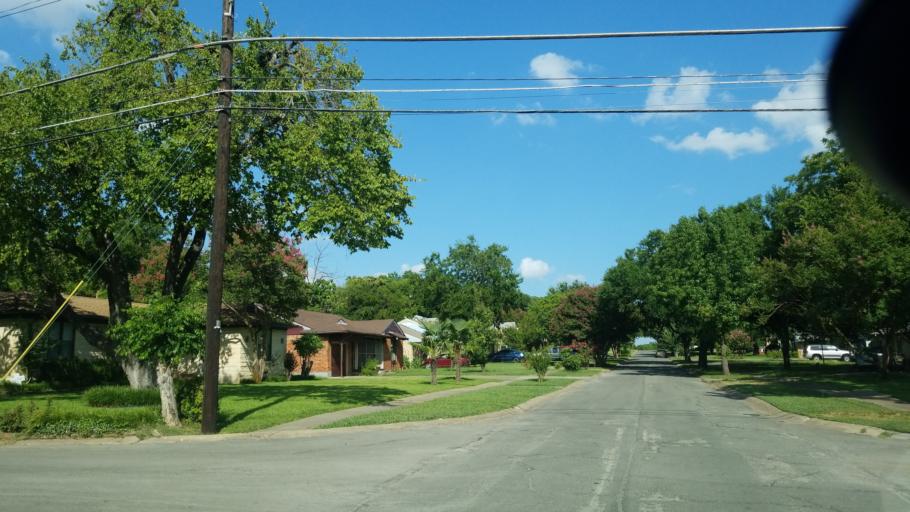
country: US
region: Texas
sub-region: Dallas County
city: Dallas
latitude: 32.7711
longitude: -96.7165
